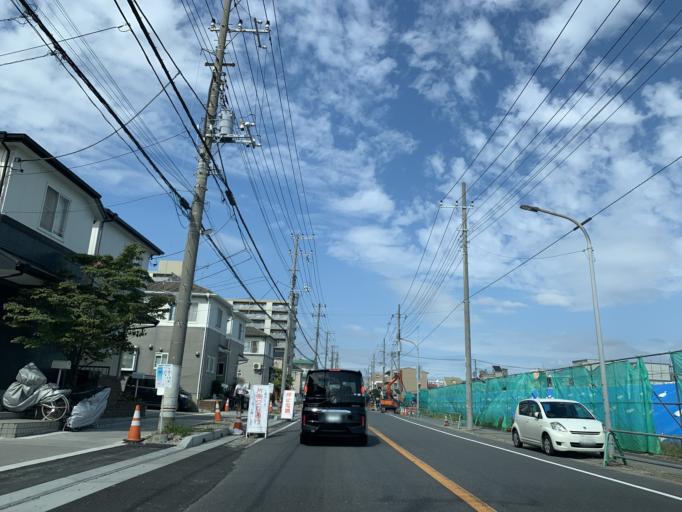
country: JP
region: Tokyo
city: Urayasu
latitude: 35.6815
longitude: 139.9311
